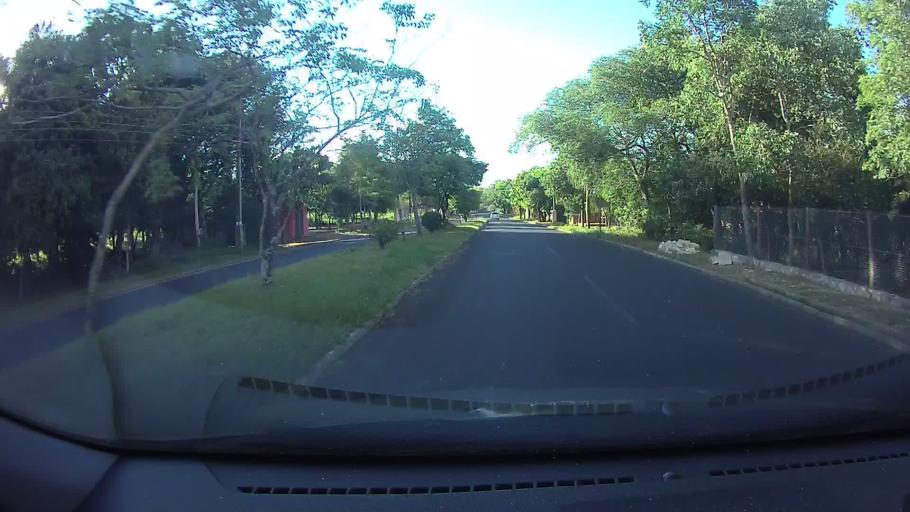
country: PY
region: Cordillera
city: Altos
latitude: -25.1685
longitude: -57.2322
